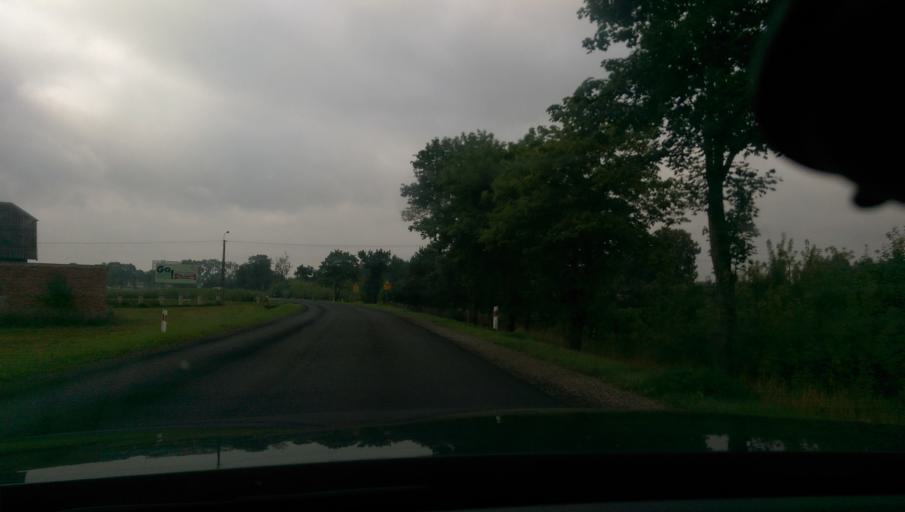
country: PL
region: Masovian Voivodeship
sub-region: Powiat przasnyski
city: Przasnysz
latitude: 53.0747
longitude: 20.8555
